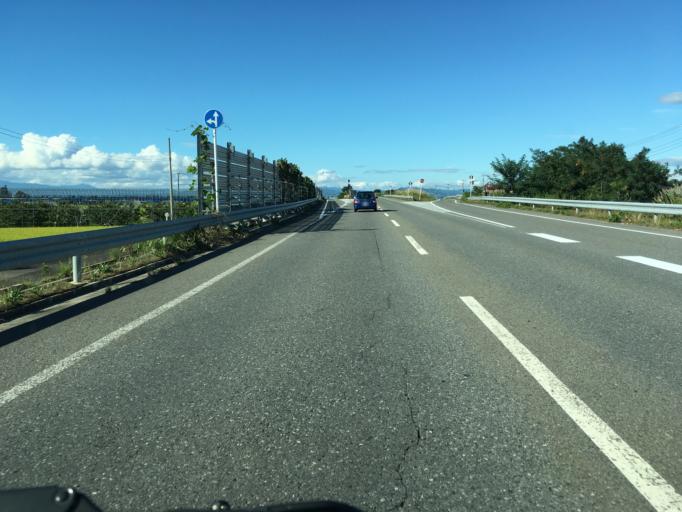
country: JP
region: Yamagata
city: Yonezawa
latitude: 37.9297
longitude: 140.1091
